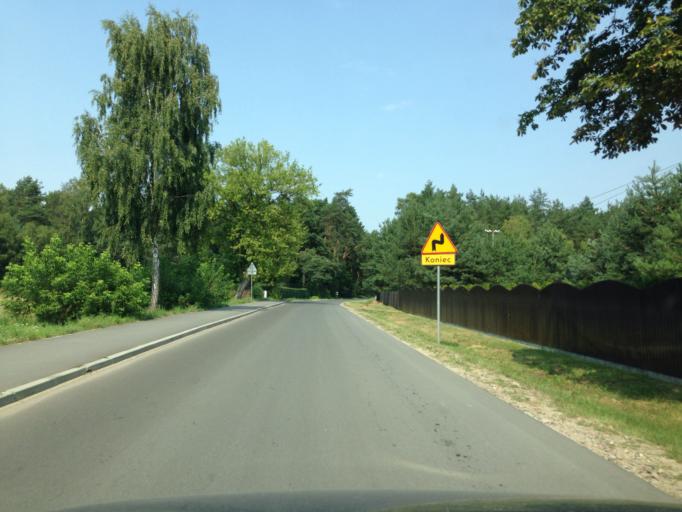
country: PL
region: Kujawsko-Pomorskie
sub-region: Powiat golubsko-dobrzynski
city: Golub-Dobrzyn
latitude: 53.0774
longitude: 19.0312
